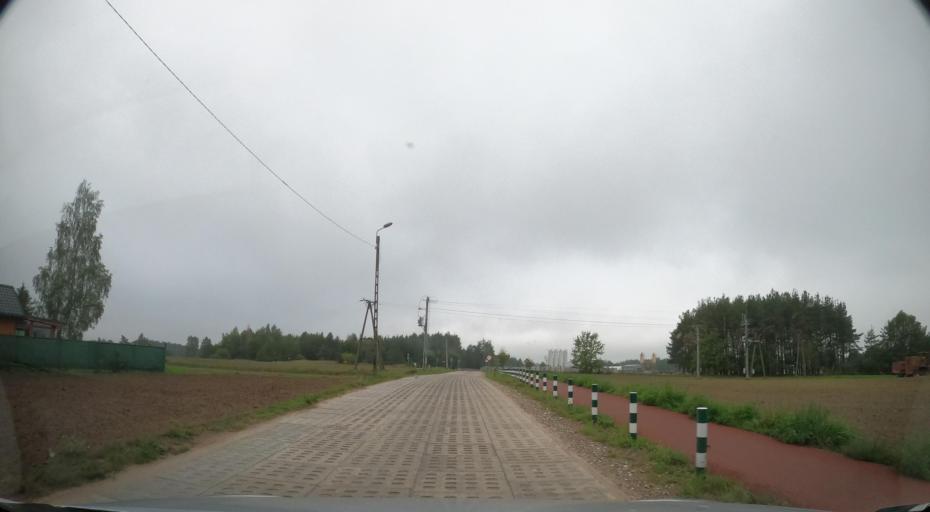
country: PL
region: Pomeranian Voivodeship
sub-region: Powiat kartuski
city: Chwaszczyno
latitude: 54.4277
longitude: 18.4159
